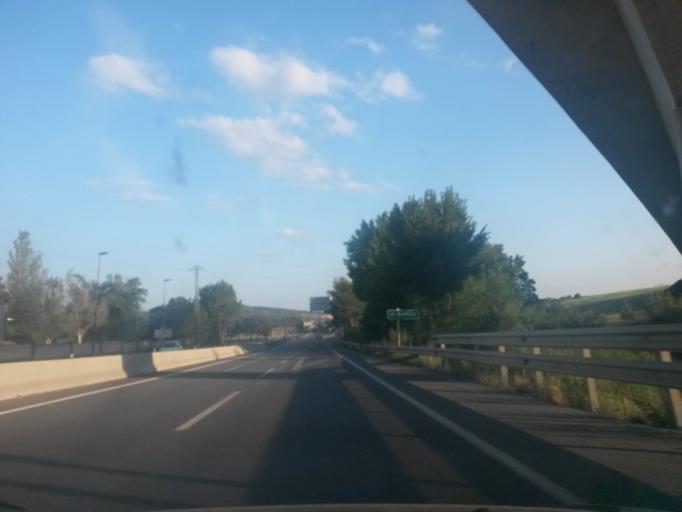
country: ES
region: Catalonia
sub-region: Provincia de Girona
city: Sarria de Ter
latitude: 42.0400
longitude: 2.8223
